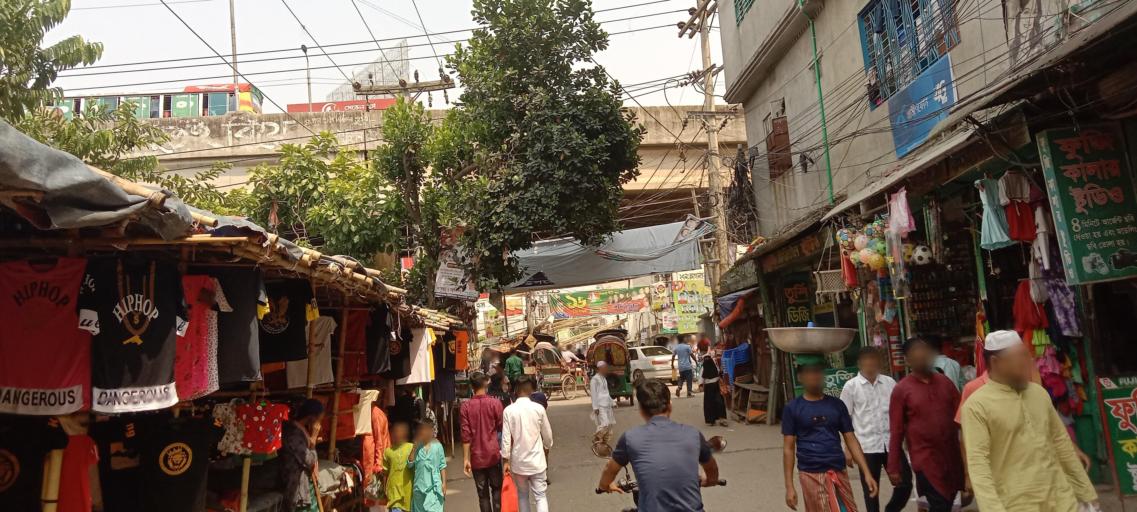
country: BD
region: Dhaka
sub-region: Dhaka
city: Dhaka
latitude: 23.7066
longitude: 90.3997
